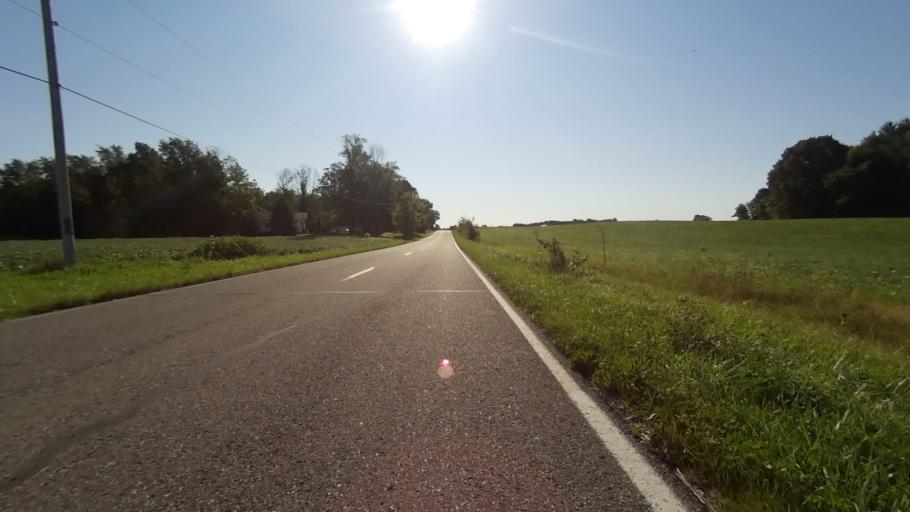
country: US
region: Ohio
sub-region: Portage County
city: Mantua
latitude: 41.2940
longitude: -81.2741
